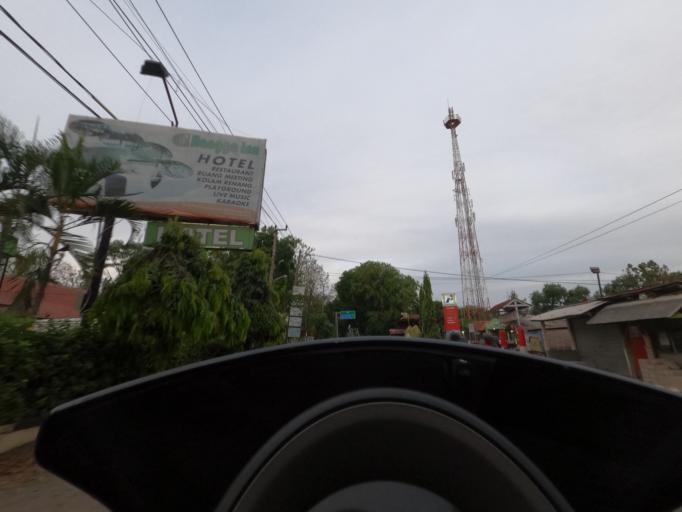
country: ID
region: West Java
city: Lembang
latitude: -6.5816
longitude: 107.7459
